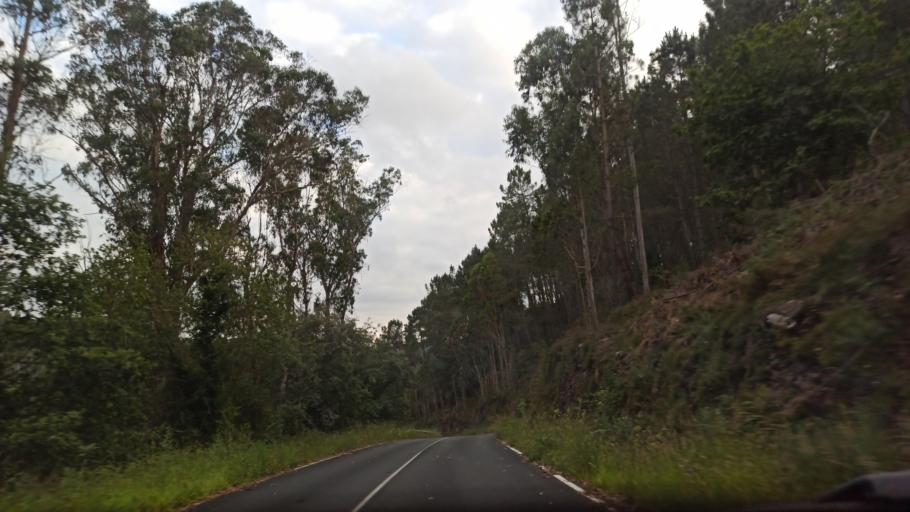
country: ES
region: Galicia
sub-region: Provincia da Coruna
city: Santiso
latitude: 42.8164
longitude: -8.1395
